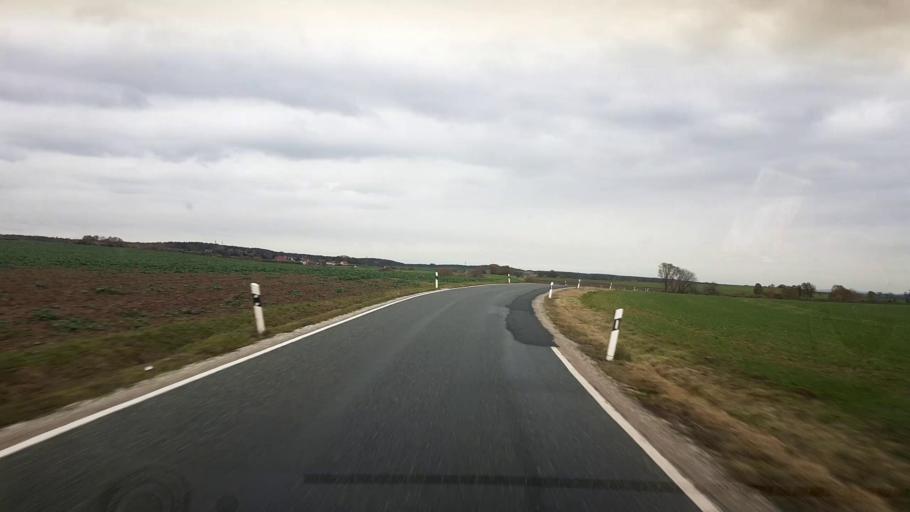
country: DE
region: Bavaria
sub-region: Upper Franconia
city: Priesendorf
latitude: 49.8611
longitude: 10.7042
